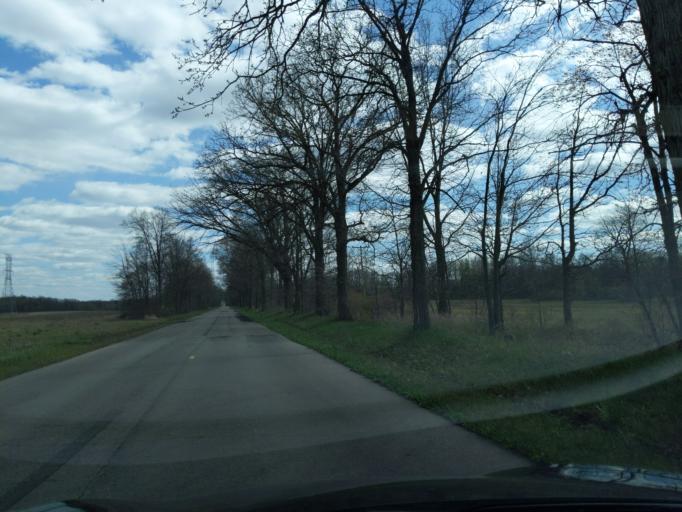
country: US
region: Michigan
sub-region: Ingham County
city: Leslie
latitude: 42.4193
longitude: -84.5267
